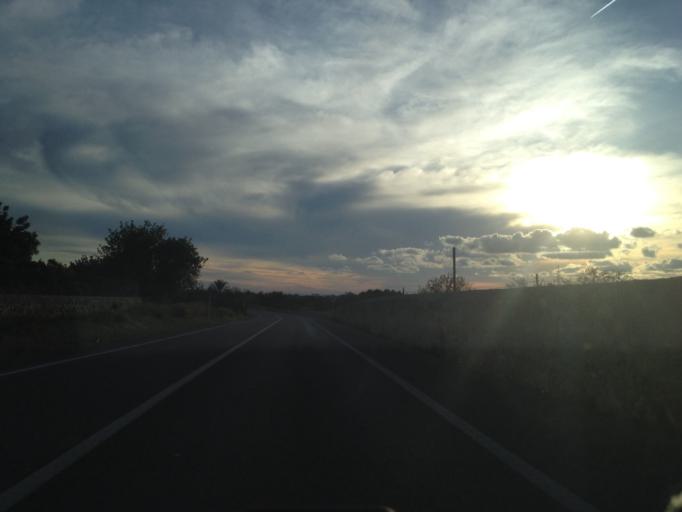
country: ES
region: Balearic Islands
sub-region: Illes Balears
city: Marratxi
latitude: 39.6440
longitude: 2.7448
